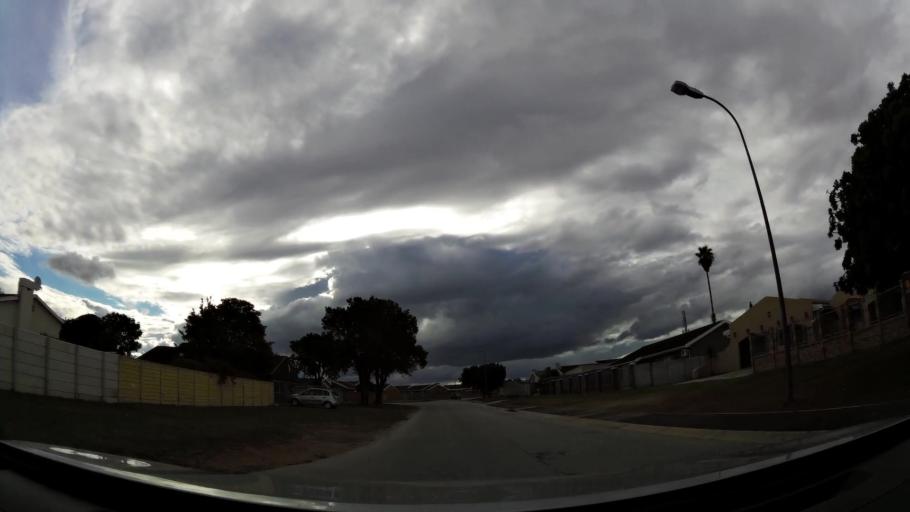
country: ZA
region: Eastern Cape
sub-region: Nelson Mandela Bay Metropolitan Municipality
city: Port Elizabeth
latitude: -33.9386
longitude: 25.4637
